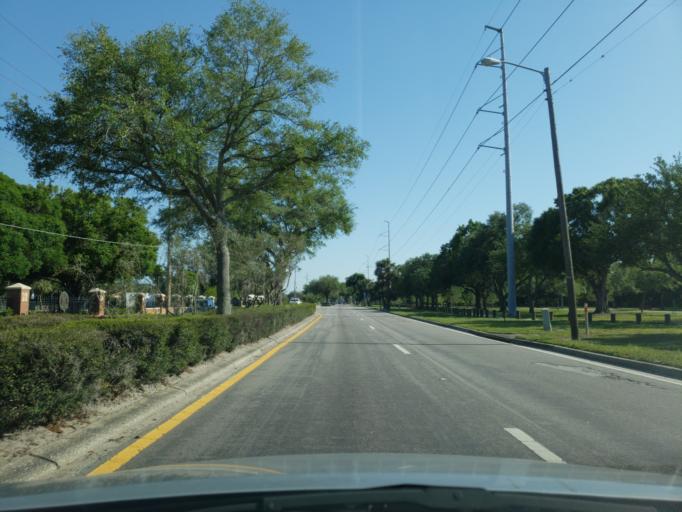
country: US
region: Florida
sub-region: Hillsborough County
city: Egypt Lake-Leto
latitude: 27.9874
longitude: -82.5012
